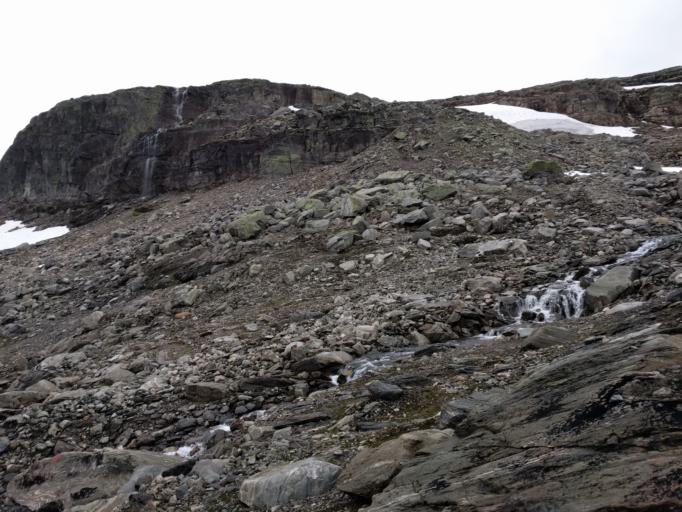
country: NO
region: Aust-Agder
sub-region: Bykle
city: Hovden
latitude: 59.8823
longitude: 7.0484
